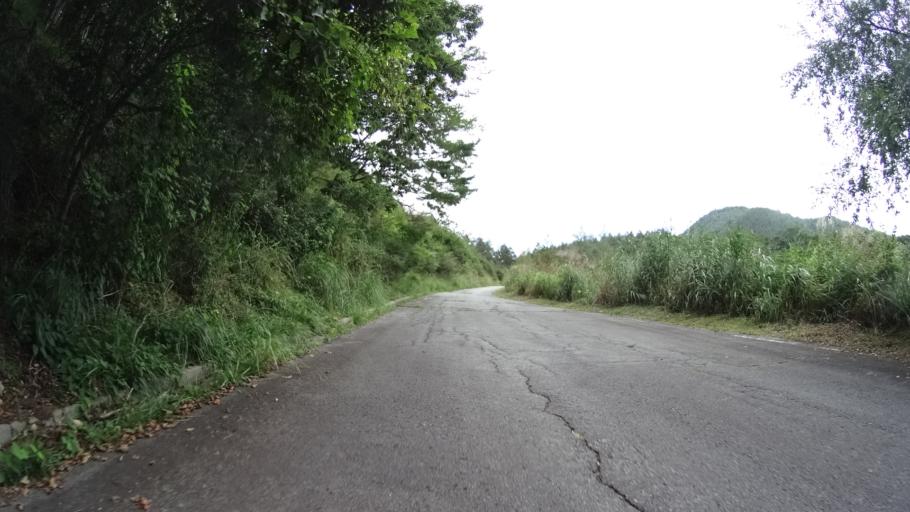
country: JP
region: Yamanashi
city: Kofu-shi
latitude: 35.8254
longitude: 138.5537
